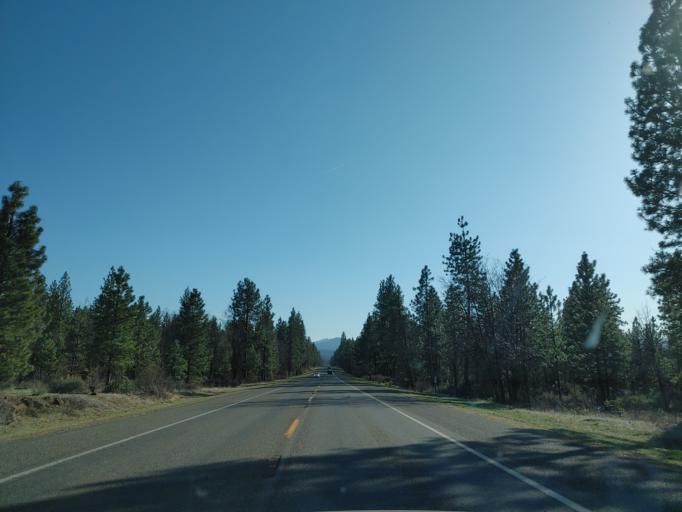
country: US
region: California
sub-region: Shasta County
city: Burney
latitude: 40.9081
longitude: -121.6361
